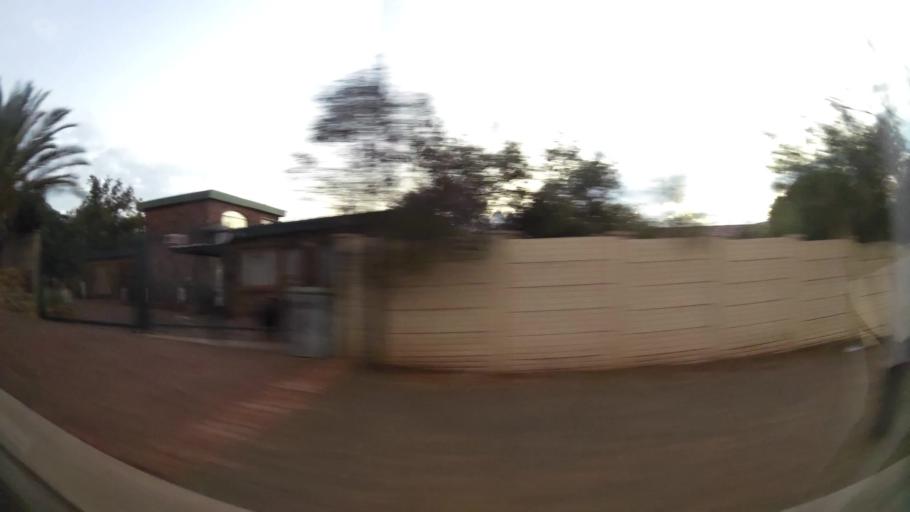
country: ZA
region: Orange Free State
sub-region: Mangaung Metropolitan Municipality
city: Bloemfontein
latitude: -29.1553
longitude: 26.1934
